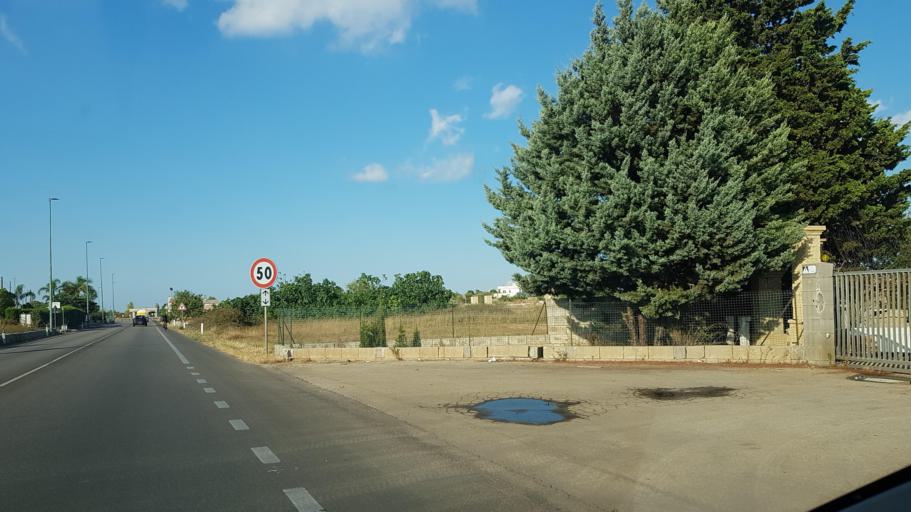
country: IT
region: Apulia
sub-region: Provincia di Lecce
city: Montesano Salentino
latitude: 39.9693
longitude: 18.3243
